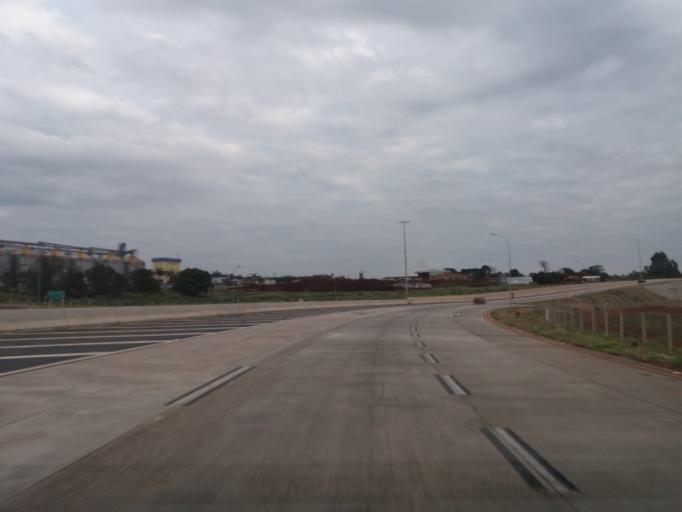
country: BR
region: Parana
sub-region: Cascavel
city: Cascavel
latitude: -25.1357
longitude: -53.5842
